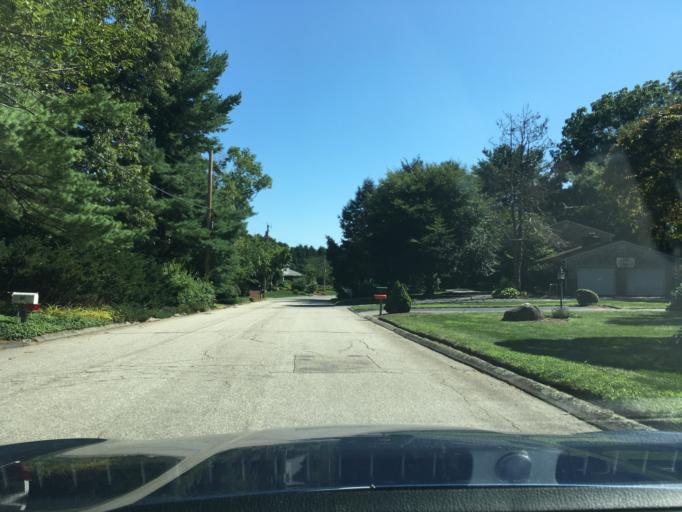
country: US
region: Rhode Island
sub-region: Kent County
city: East Greenwich
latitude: 41.6345
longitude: -71.4738
